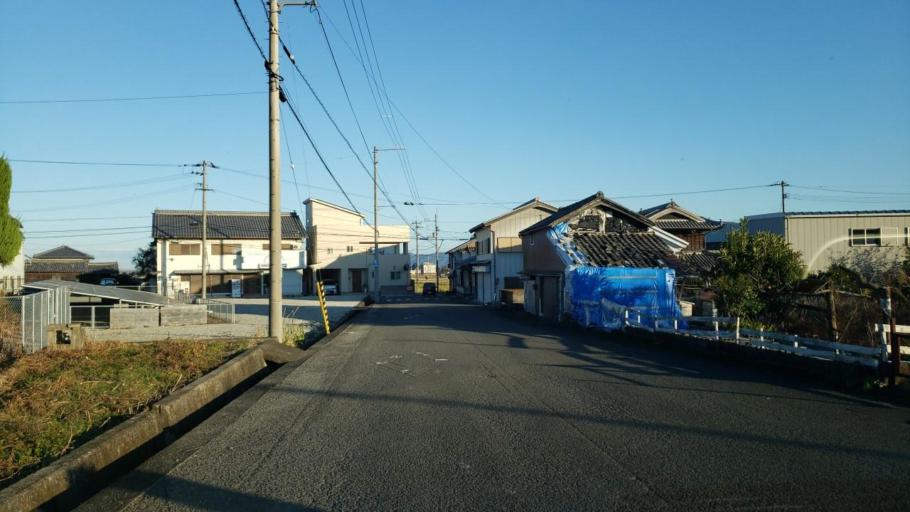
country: JP
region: Tokushima
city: Kamojimacho-jogejima
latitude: 34.0911
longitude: 134.2541
